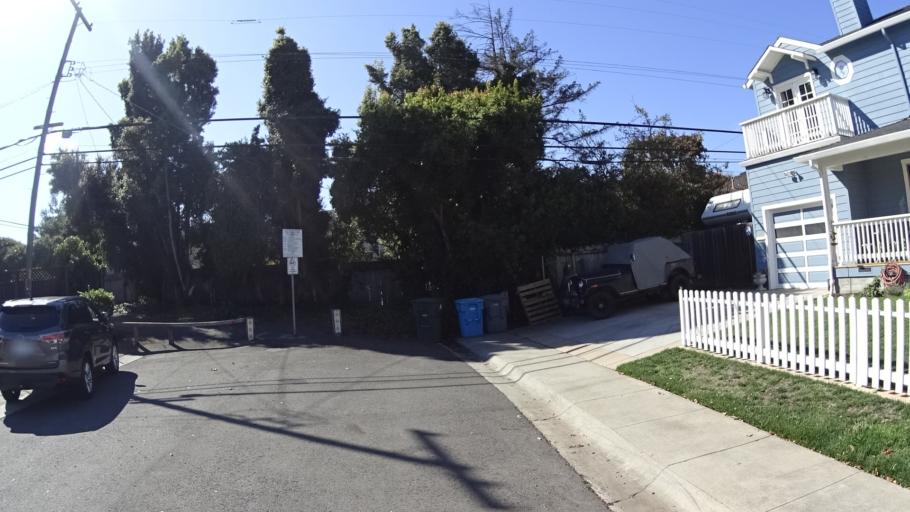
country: US
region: California
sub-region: San Mateo County
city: San Bruno
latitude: 37.6225
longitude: -122.4215
